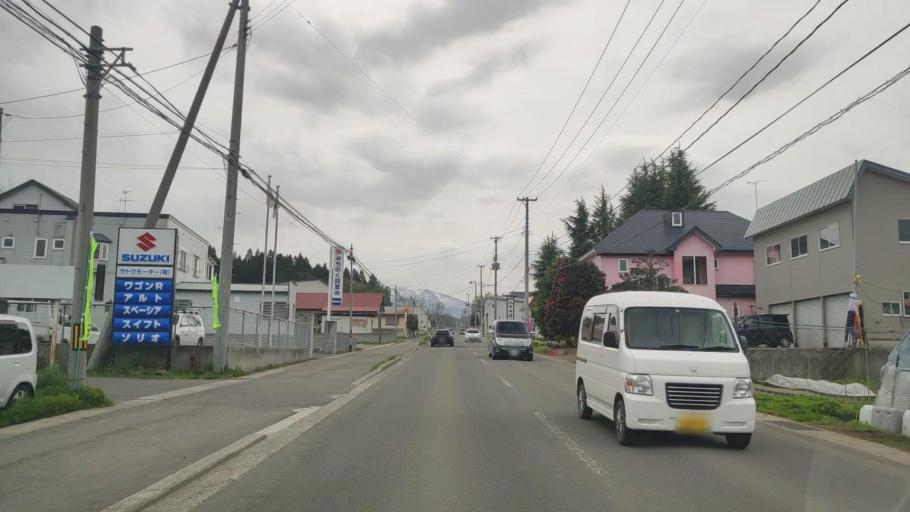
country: JP
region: Aomori
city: Aomori Shi
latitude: 40.7828
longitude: 140.7913
